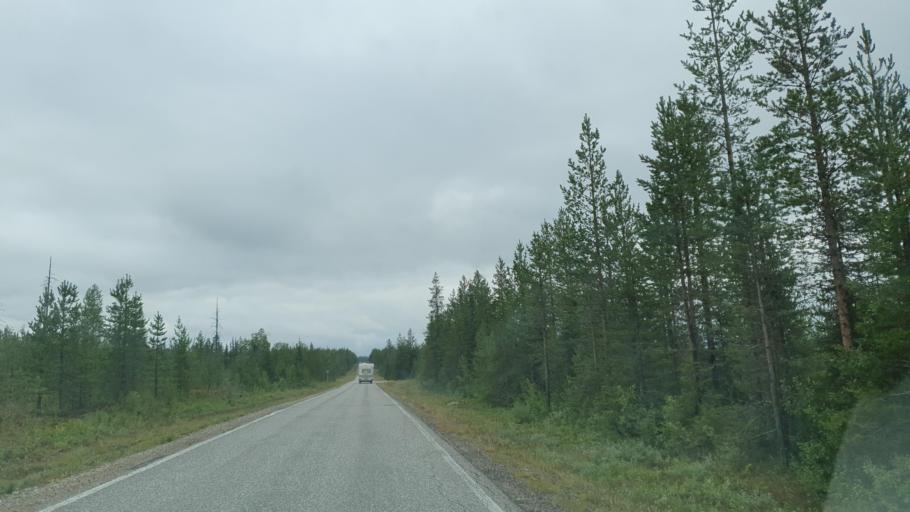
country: FI
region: Lapland
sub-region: Tunturi-Lappi
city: Muonio
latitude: 67.8159
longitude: 24.0683
